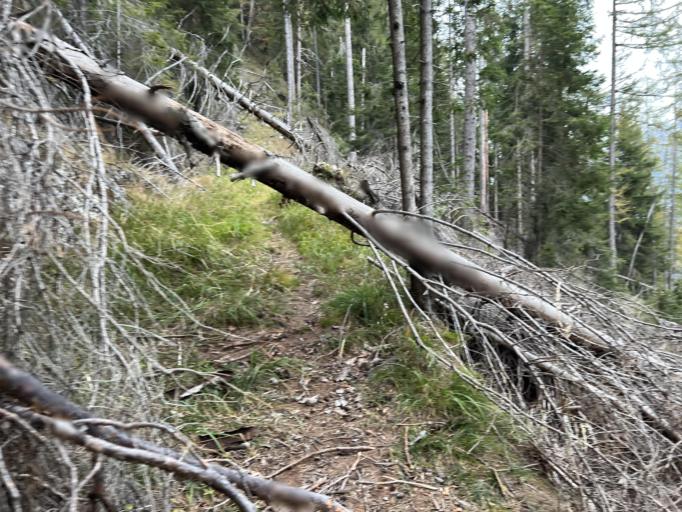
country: IT
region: Veneto
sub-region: Provincia di Belluno
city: San Pietro di Cadore
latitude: 46.5846
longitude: 12.6332
